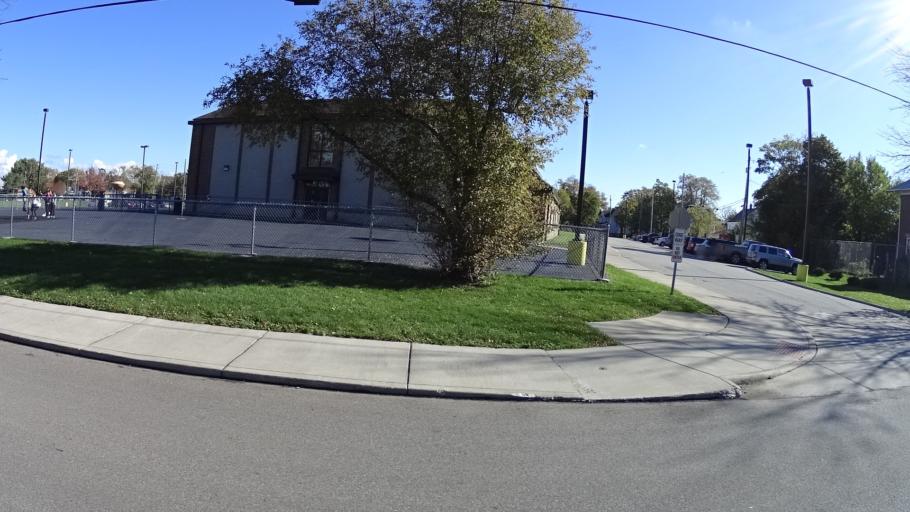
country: US
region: Ohio
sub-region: Lorain County
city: Lorain
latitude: 41.4628
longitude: -82.1810
